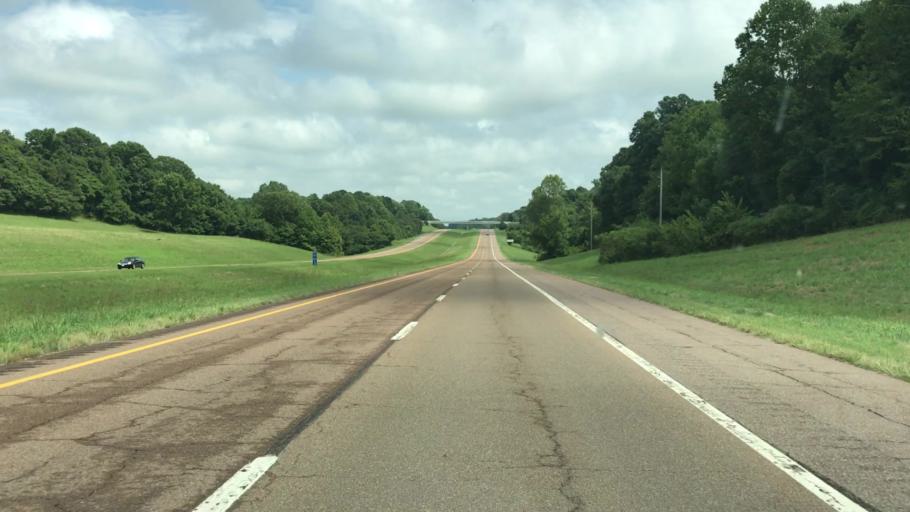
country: US
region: Tennessee
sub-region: Dyer County
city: Dyersburg
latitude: 36.0711
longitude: -89.4608
